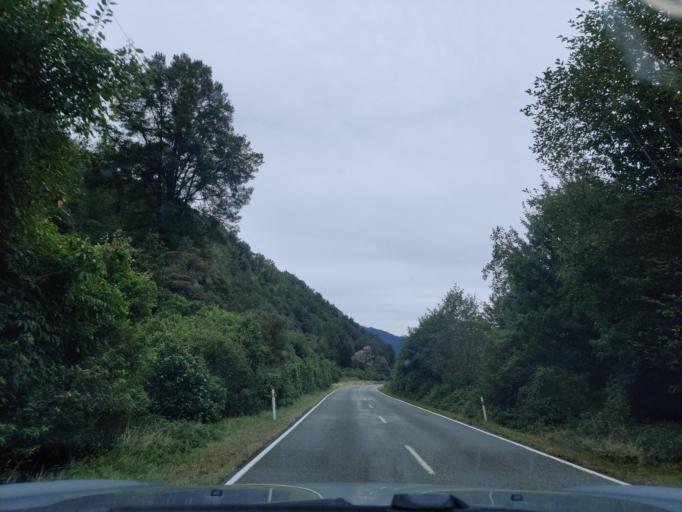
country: NZ
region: West Coast
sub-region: Buller District
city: Westport
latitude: -41.7819
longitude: 172.2101
